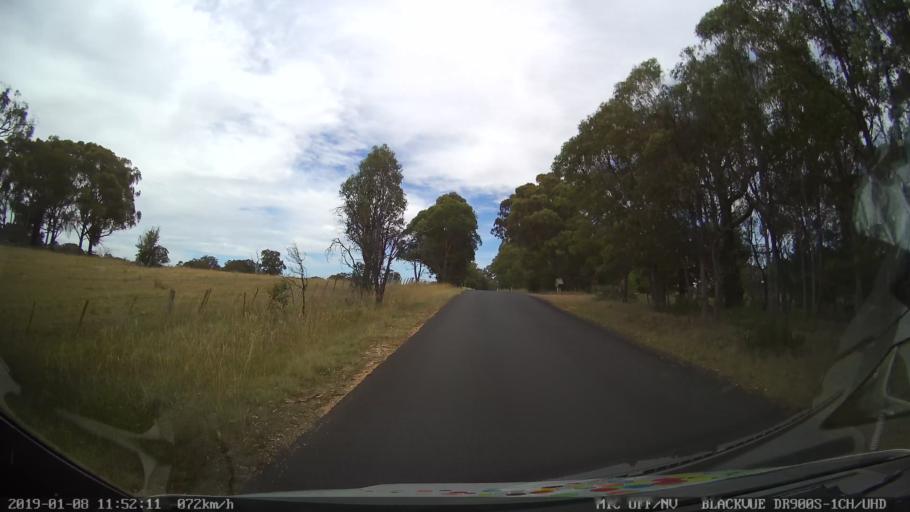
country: AU
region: New South Wales
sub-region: Armidale Dumaresq
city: Armidale
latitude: -30.4012
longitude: 151.5609
